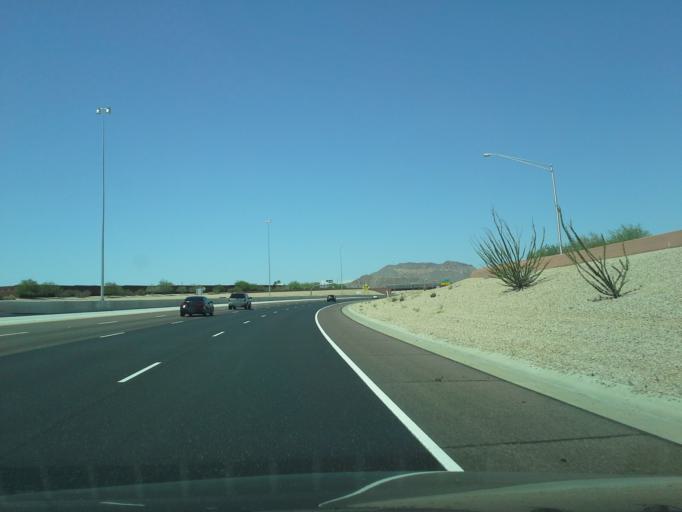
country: US
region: Arizona
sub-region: Pinal County
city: Apache Junction
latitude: 33.4101
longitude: -111.6399
